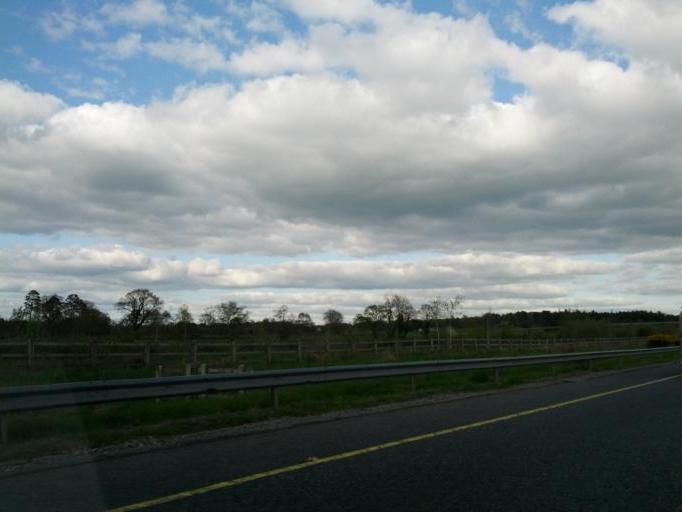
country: IE
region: Leinster
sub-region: An Iarmhi
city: Athlone
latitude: 53.4023
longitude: -7.8654
